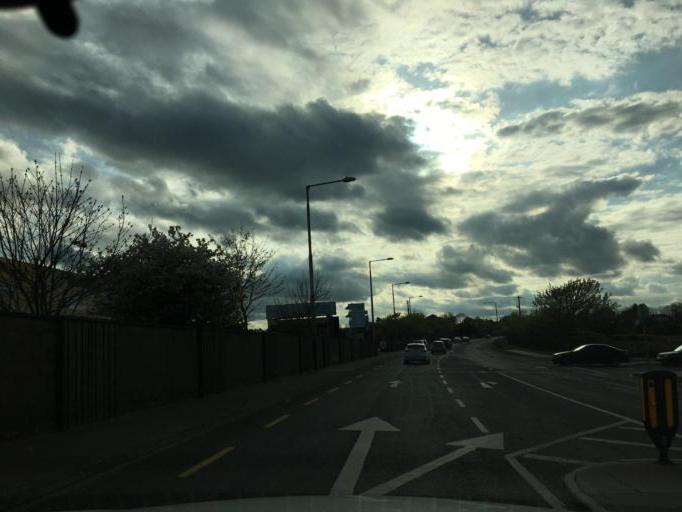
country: IE
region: Leinster
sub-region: Loch Garman
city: Loch Garman
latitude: 52.3413
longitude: -6.4910
